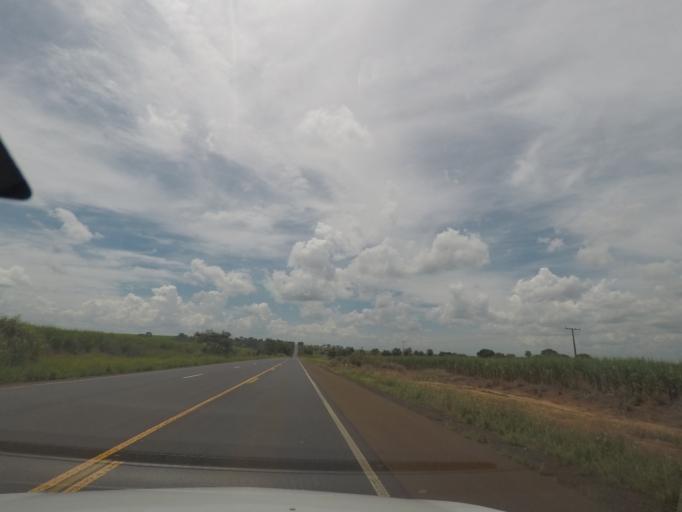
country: BR
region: Sao Paulo
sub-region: Barretos
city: Barretos
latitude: -20.4105
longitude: -48.6337
